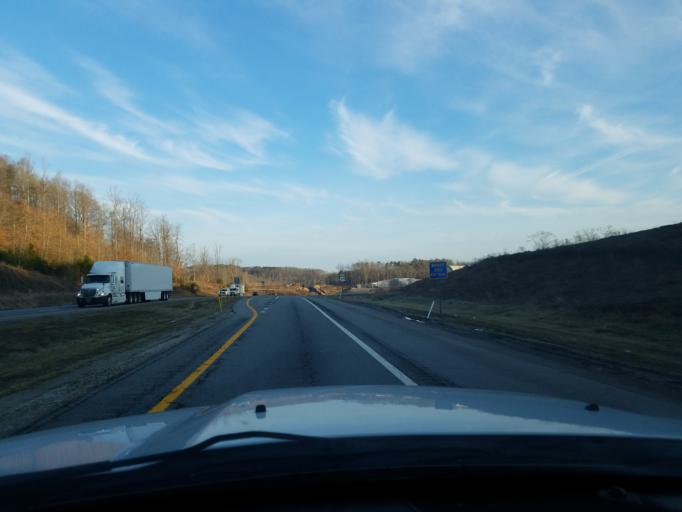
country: US
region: West Virginia
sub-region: Putnam County
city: Buffalo
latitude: 38.5750
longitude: -82.0154
